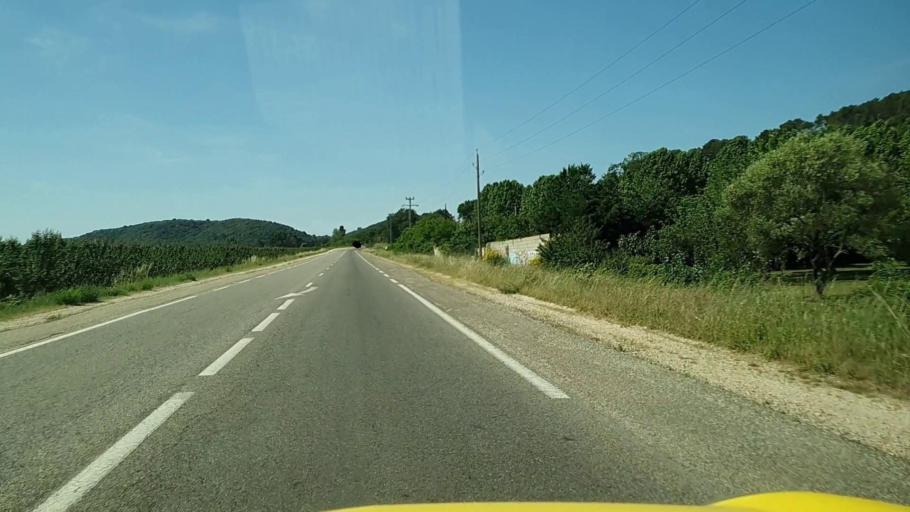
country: FR
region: Languedoc-Roussillon
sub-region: Departement du Gard
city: Connaux
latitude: 44.0847
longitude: 4.5935
